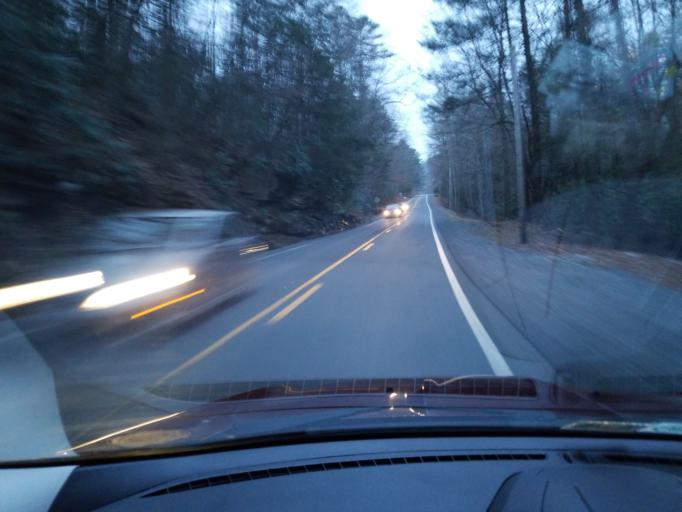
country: US
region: West Virginia
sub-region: Greenbrier County
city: Fairlea
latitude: 37.7576
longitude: -80.3980
